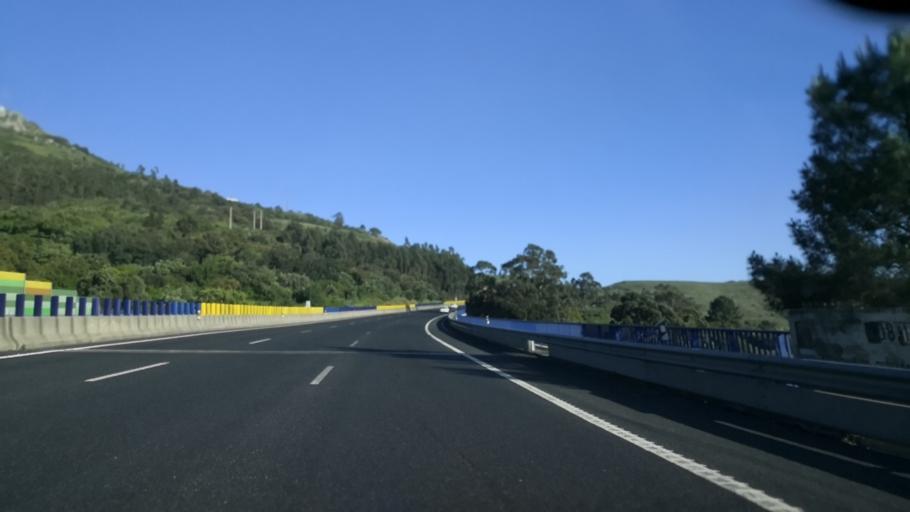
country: PT
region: Lisbon
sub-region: Mafra
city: Venda do Pinheiro
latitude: 38.9007
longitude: -9.2014
